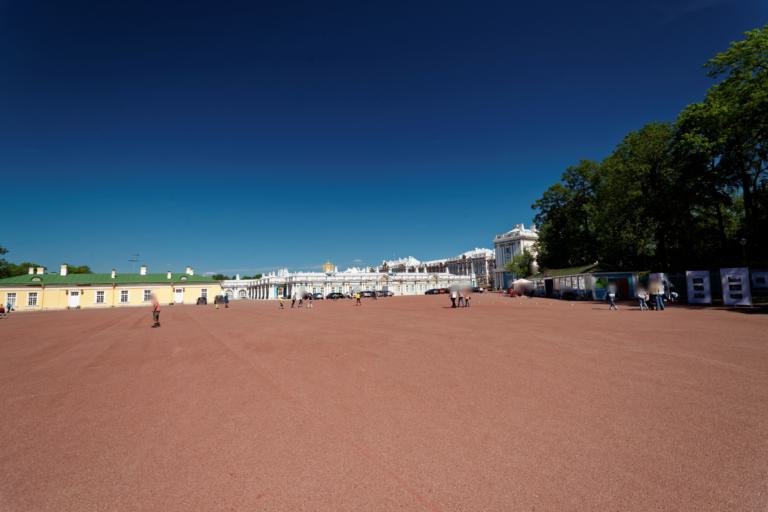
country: RU
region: St.-Petersburg
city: Pushkin
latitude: 59.7149
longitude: 30.3903
